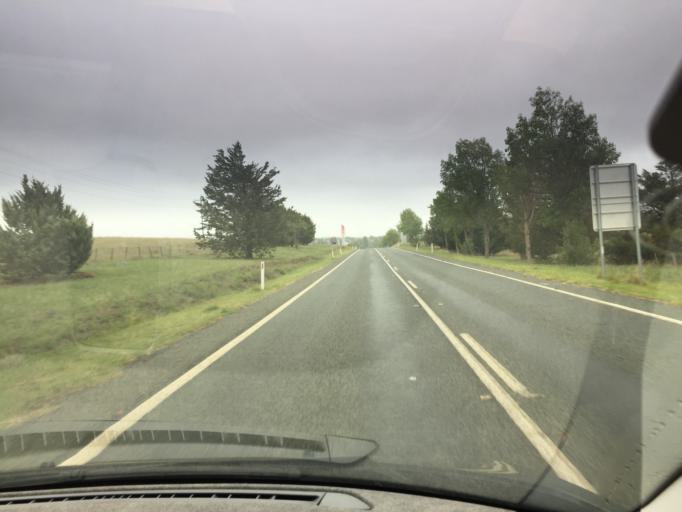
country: AU
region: New South Wales
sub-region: Cooma-Monaro
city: Cooma
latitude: -36.2141
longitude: 149.1491
